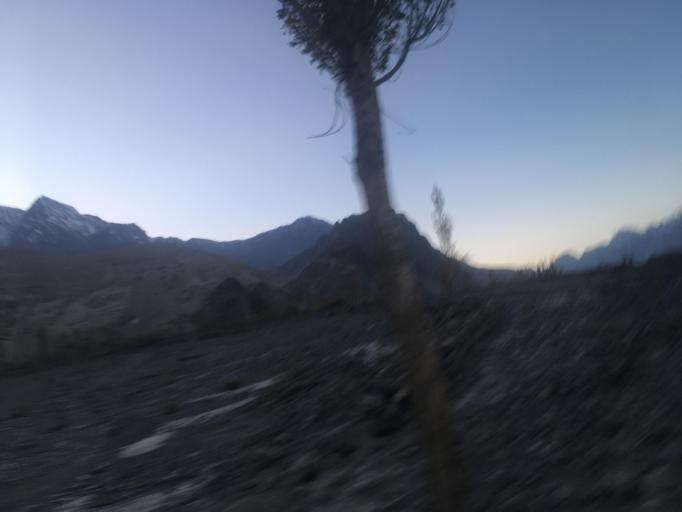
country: PK
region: Gilgit-Baltistan
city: Skardu
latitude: 35.3040
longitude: 75.5374
